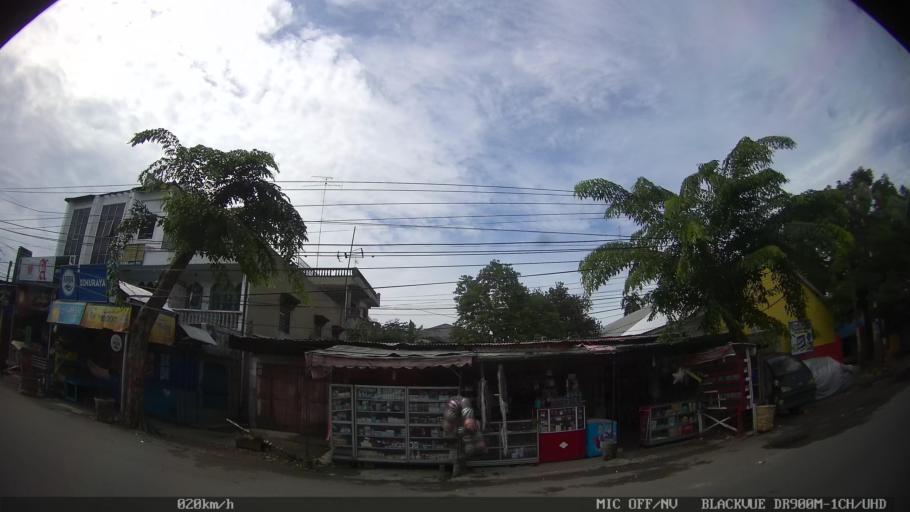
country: ID
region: North Sumatra
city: Medan
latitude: 3.6226
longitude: 98.6815
